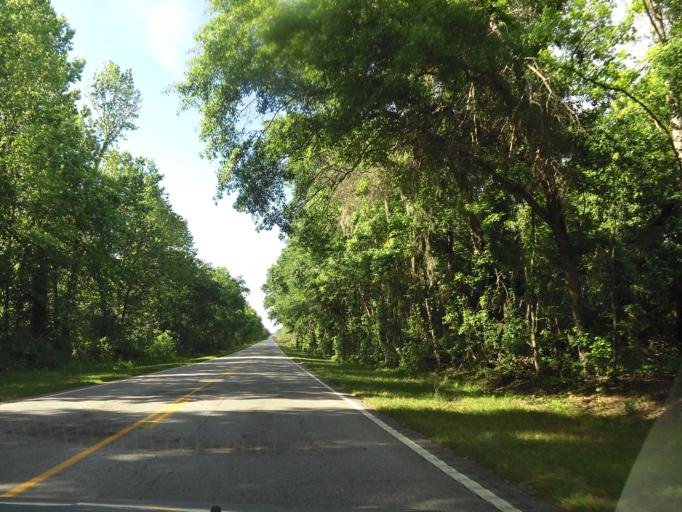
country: US
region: South Carolina
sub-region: Allendale County
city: Fairfax
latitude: 32.8993
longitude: -81.2379
